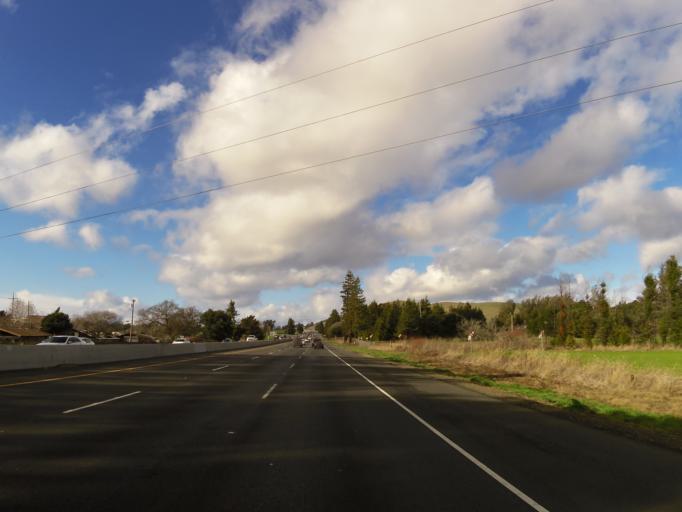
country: US
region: California
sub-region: Sonoma County
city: Penngrove
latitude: 38.2795
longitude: -122.6795
